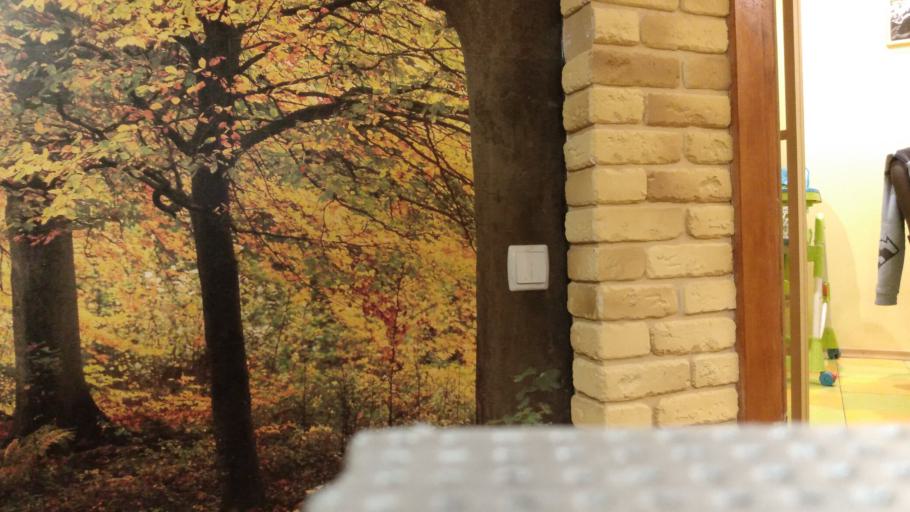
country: RU
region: Vologda
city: Babayevo
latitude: 59.3730
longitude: 35.9931
